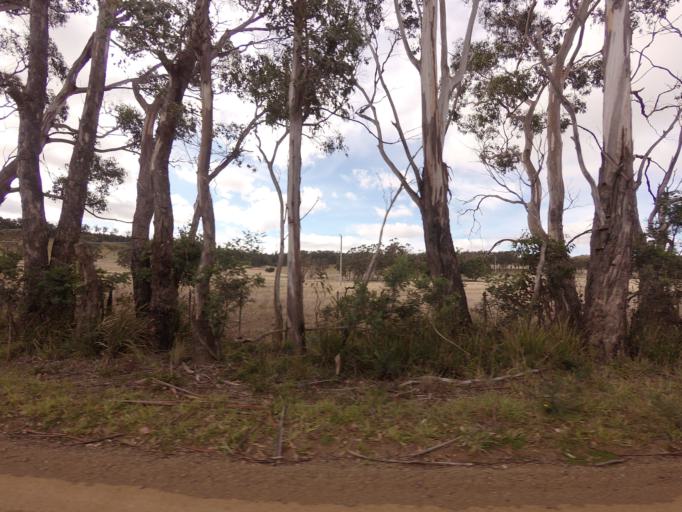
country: AU
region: Tasmania
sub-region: Brighton
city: Bridgewater
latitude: -42.4222
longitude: 147.4235
